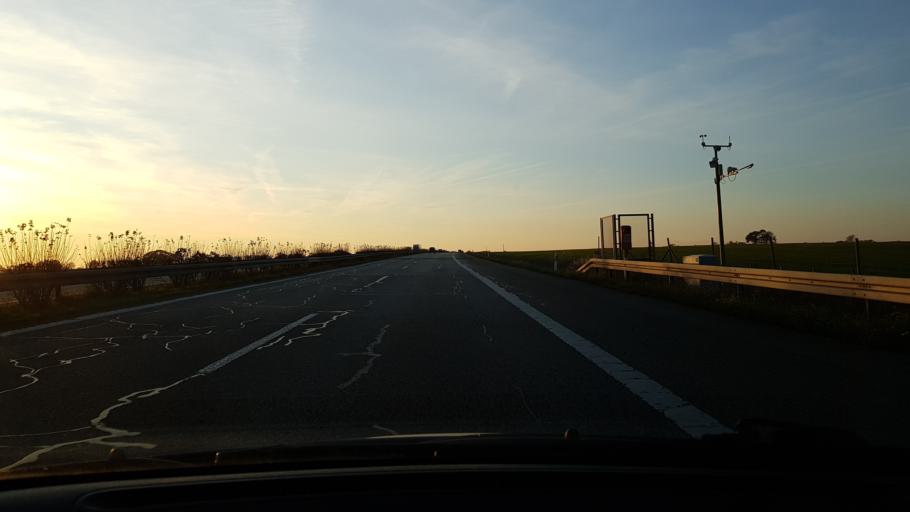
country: DE
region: Mecklenburg-Vorpommern
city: Hagenow
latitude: 53.4862
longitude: 11.2001
